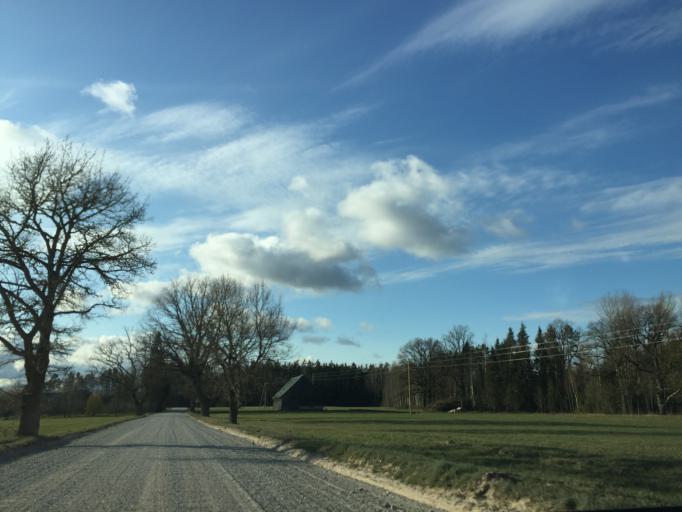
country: LV
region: Burtnieki
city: Matisi
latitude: 57.6215
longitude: 25.0688
